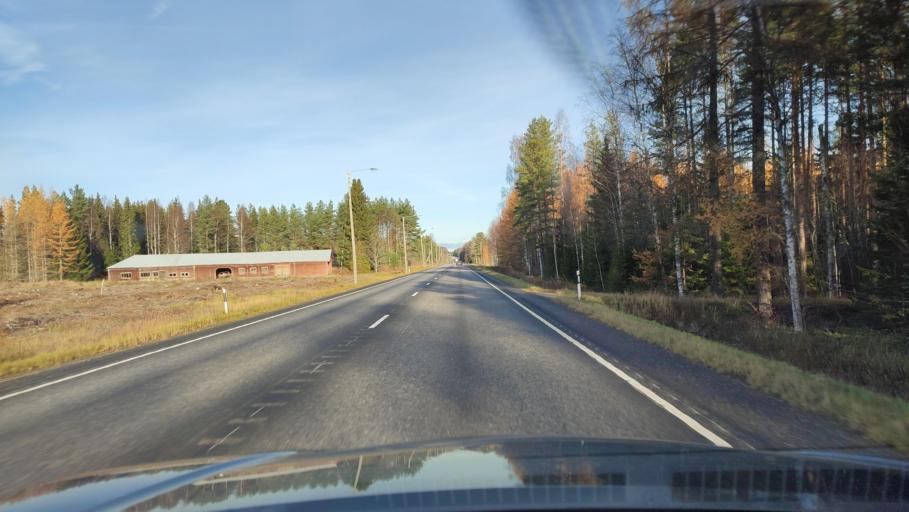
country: FI
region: Ostrobothnia
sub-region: Vaasa
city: Malax
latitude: 62.8031
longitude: 21.6780
